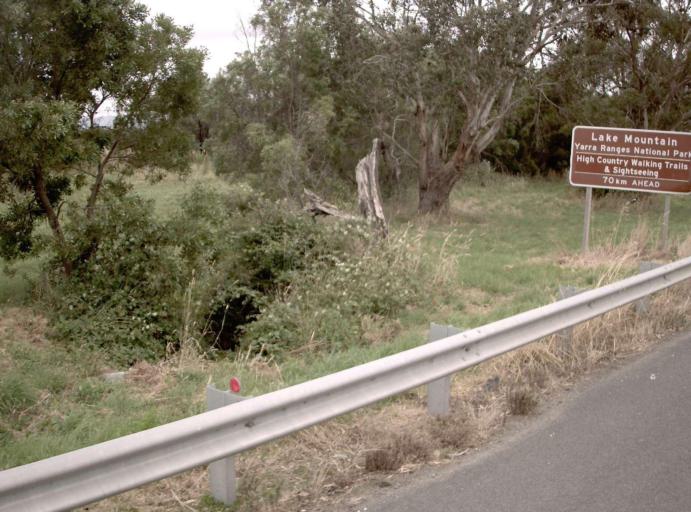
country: AU
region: Victoria
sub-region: Yarra Ranges
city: Yarra Glen
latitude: -37.7097
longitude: 145.3978
